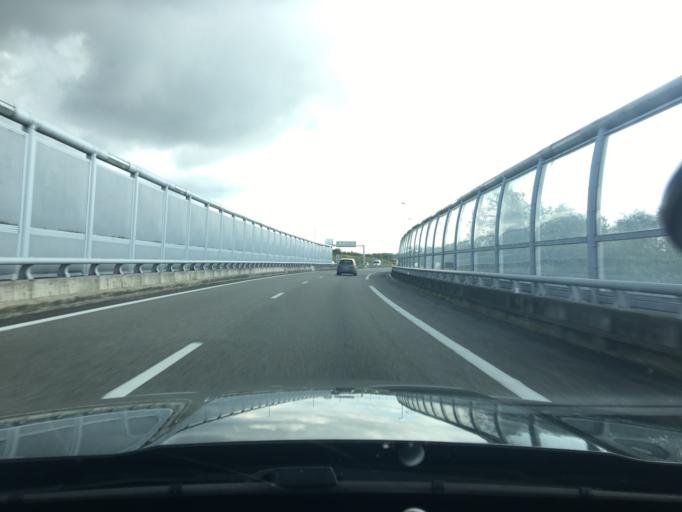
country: FR
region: Ile-de-France
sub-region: Departement des Yvelines
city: Montesson
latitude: 48.9177
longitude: 2.1202
